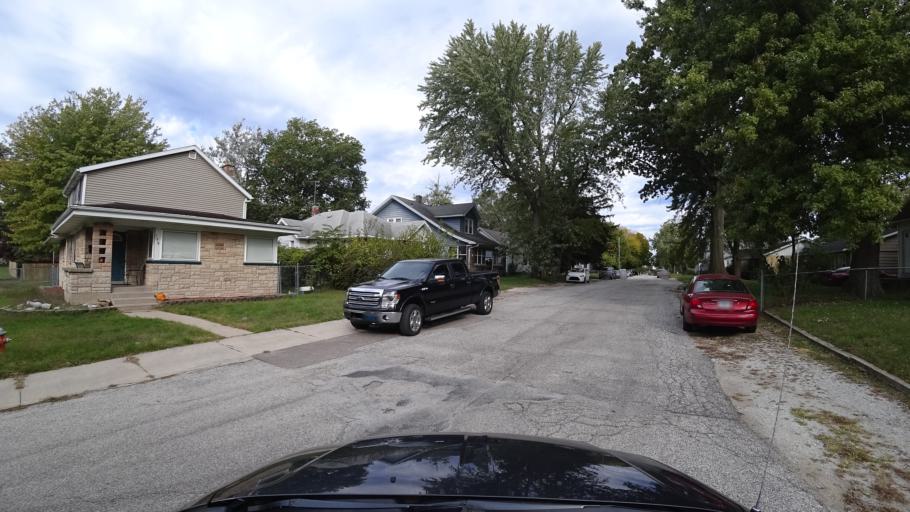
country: US
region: Indiana
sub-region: LaPorte County
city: Trail Creek
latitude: 41.7076
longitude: -86.8735
